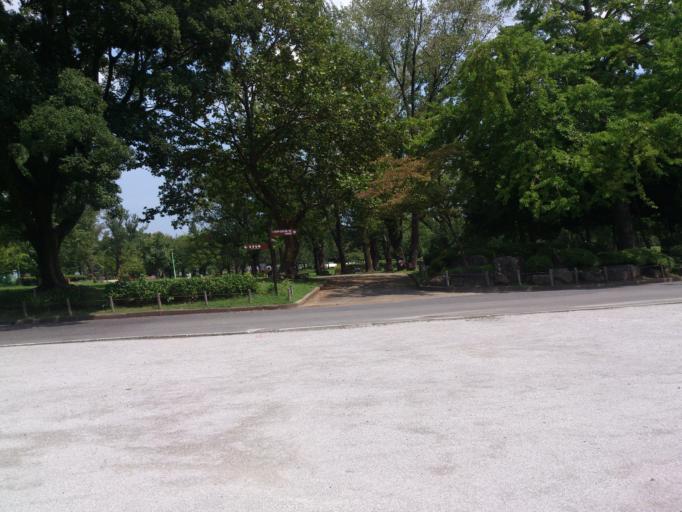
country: JP
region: Shizuoka
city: Shizuoka-shi
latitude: 34.9783
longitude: 138.3823
